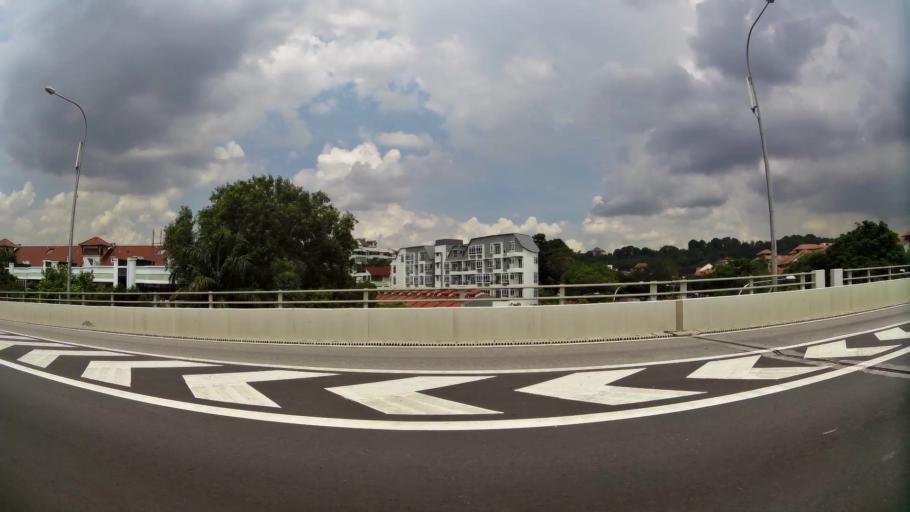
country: SG
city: Singapore
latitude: 1.2784
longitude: 103.7856
